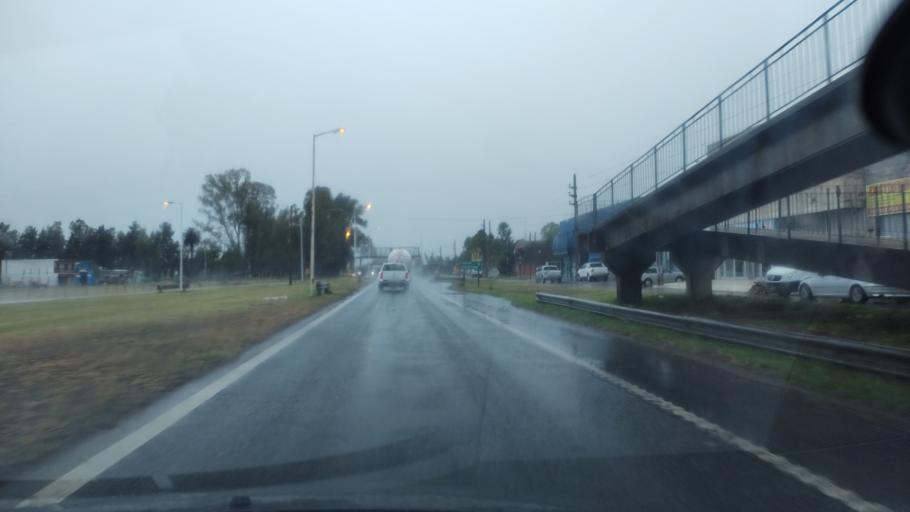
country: AR
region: Buenos Aires
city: Canuelas
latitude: -35.0456
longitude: -58.7673
